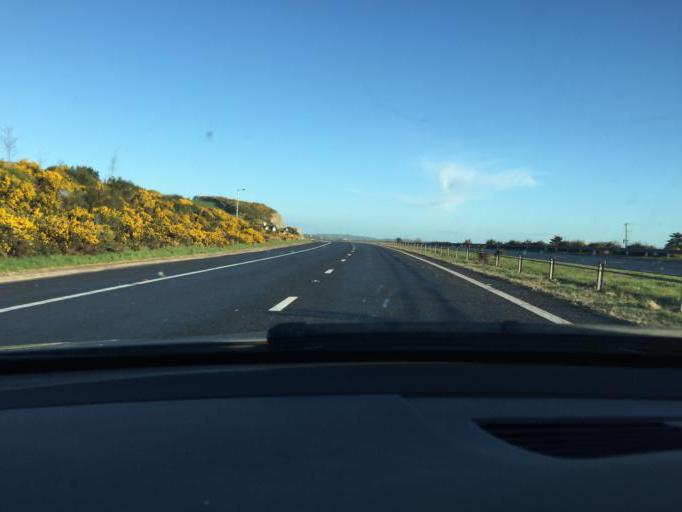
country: GB
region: Northern Ireland
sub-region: Newry and Mourne District
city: Newry
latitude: 54.1493
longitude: -6.3450
